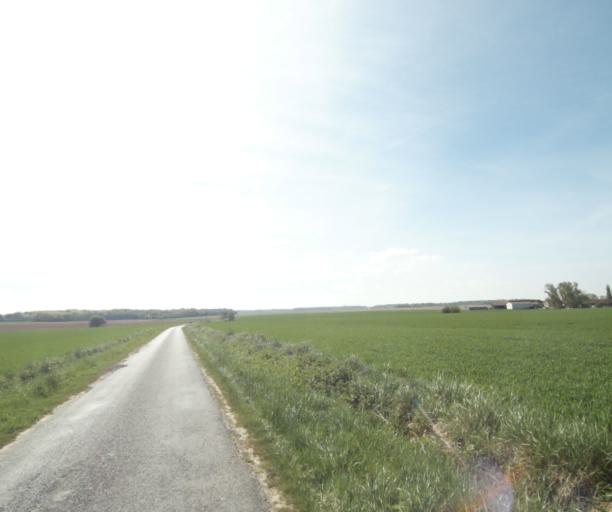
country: FR
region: Ile-de-France
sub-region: Departement de Seine-et-Marne
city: Nangis
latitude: 48.5494
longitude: 3.0334
